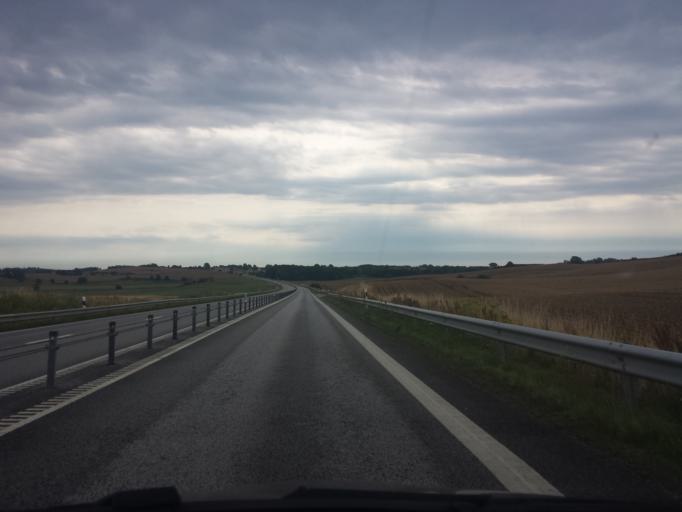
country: SE
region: Skane
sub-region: Ystads Kommun
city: Ystad
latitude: 55.4644
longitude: 13.7176
